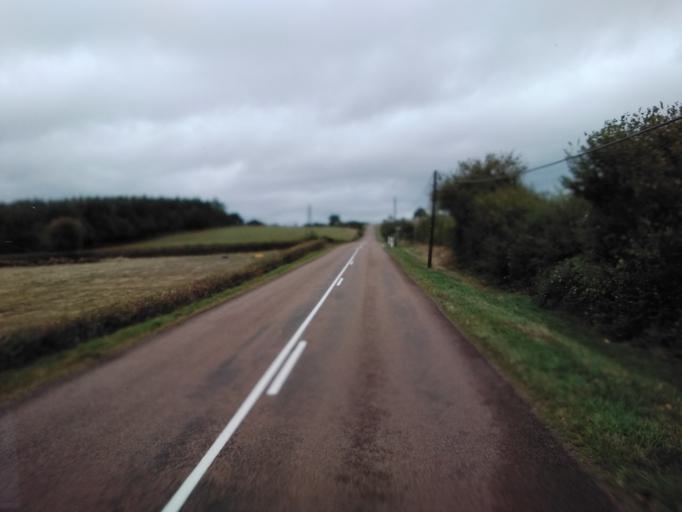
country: FR
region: Bourgogne
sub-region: Departement de la Cote-d'Or
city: Saulieu
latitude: 47.2627
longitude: 4.2079
